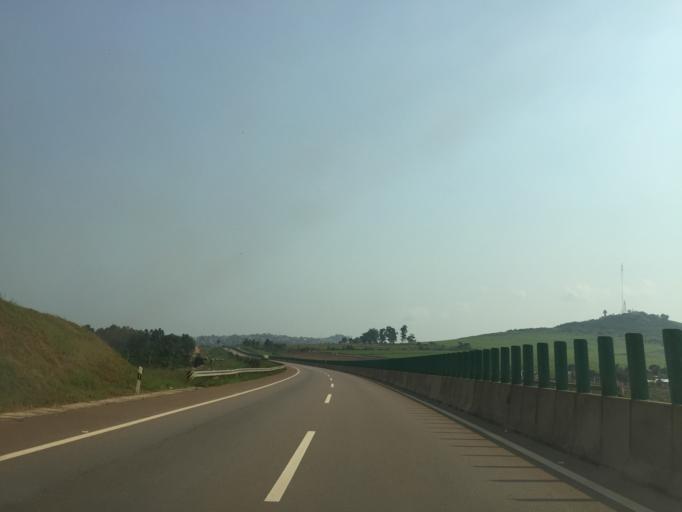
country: UG
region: Central Region
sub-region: Wakiso District
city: Kajansi
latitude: 0.2313
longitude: 32.5239
